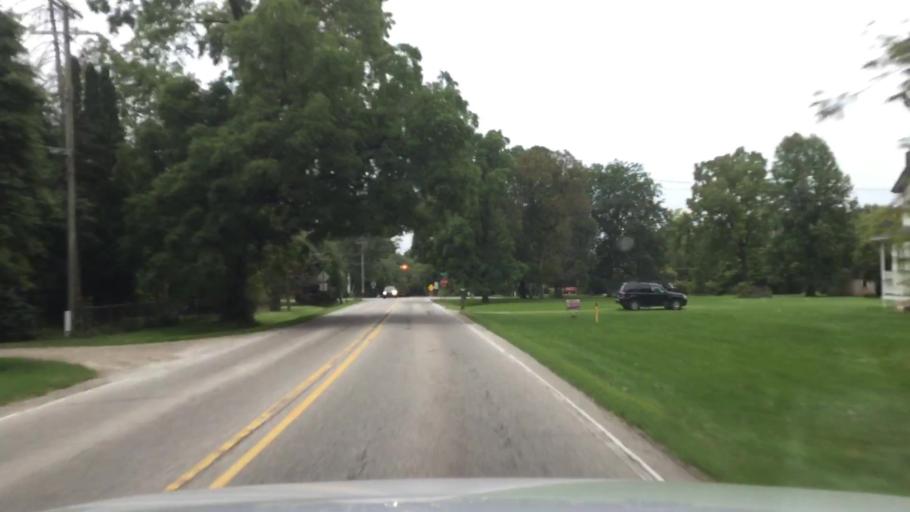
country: US
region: Michigan
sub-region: Washtenaw County
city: Milan
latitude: 42.1044
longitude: -83.7337
